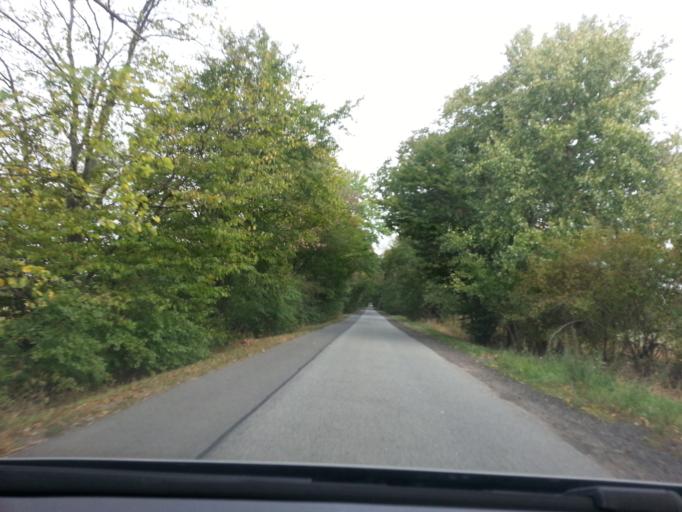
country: DE
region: Mecklenburg-Vorpommern
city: Ferdinandshof
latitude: 53.6524
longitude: 13.9192
